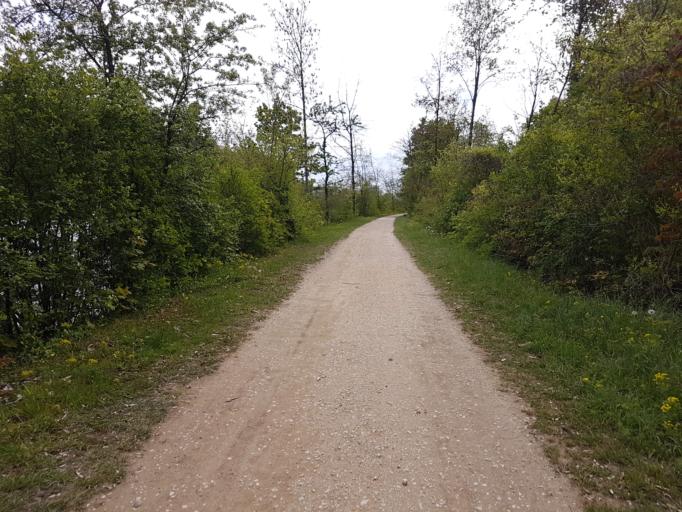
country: CH
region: Aargau
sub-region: Bezirk Brugg
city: Schinznach Bad
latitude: 47.4419
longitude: 8.1646
